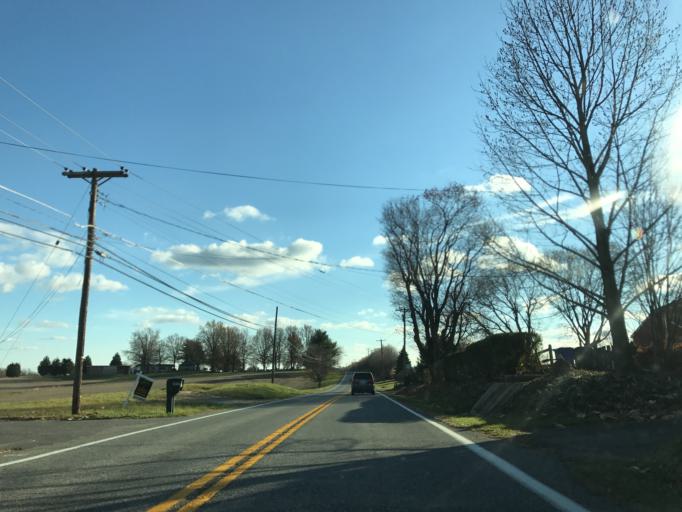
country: US
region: Maryland
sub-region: Harford County
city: Jarrettsville
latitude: 39.5737
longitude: -76.4998
